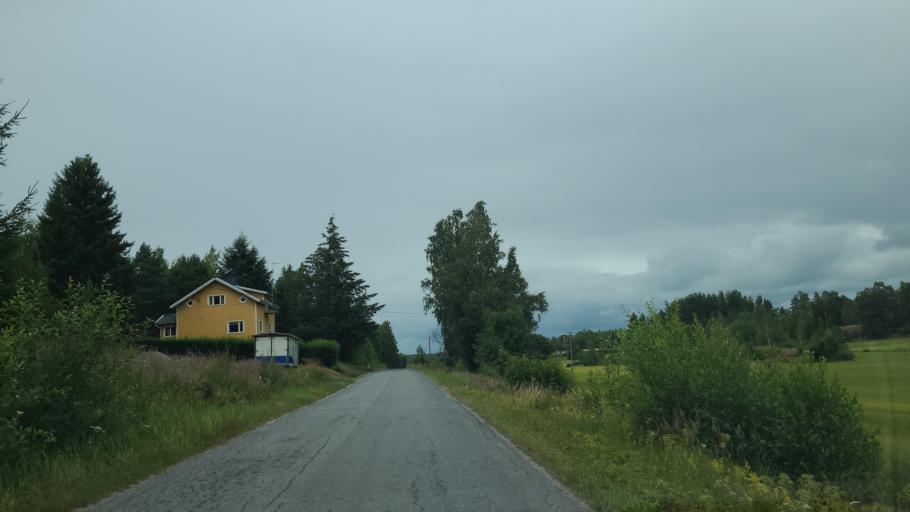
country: FI
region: Varsinais-Suomi
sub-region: Aboland-Turunmaa
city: Dragsfjaerd
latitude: 60.0925
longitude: 22.4347
